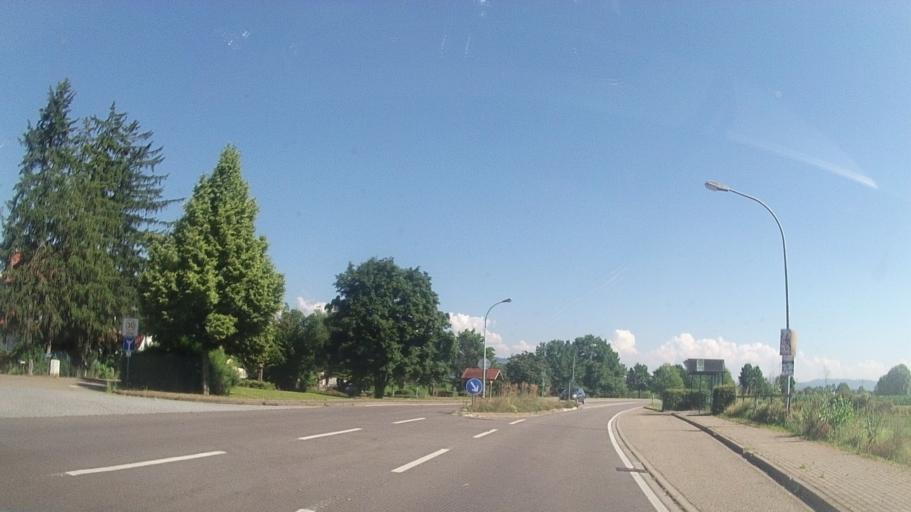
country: DE
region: Baden-Wuerttemberg
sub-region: Freiburg Region
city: Offenburg
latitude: 48.5069
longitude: 7.9279
